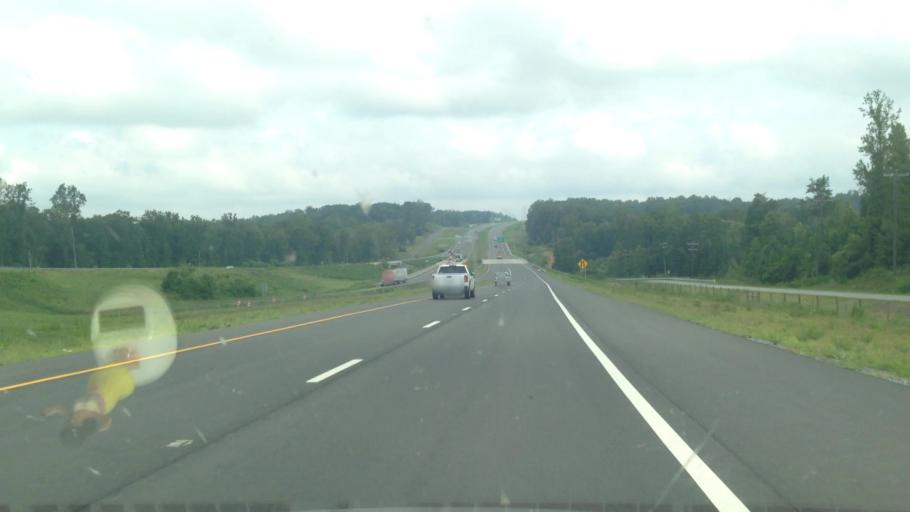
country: US
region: North Carolina
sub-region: Guilford County
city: Summerfield
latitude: 36.2244
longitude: -79.9120
